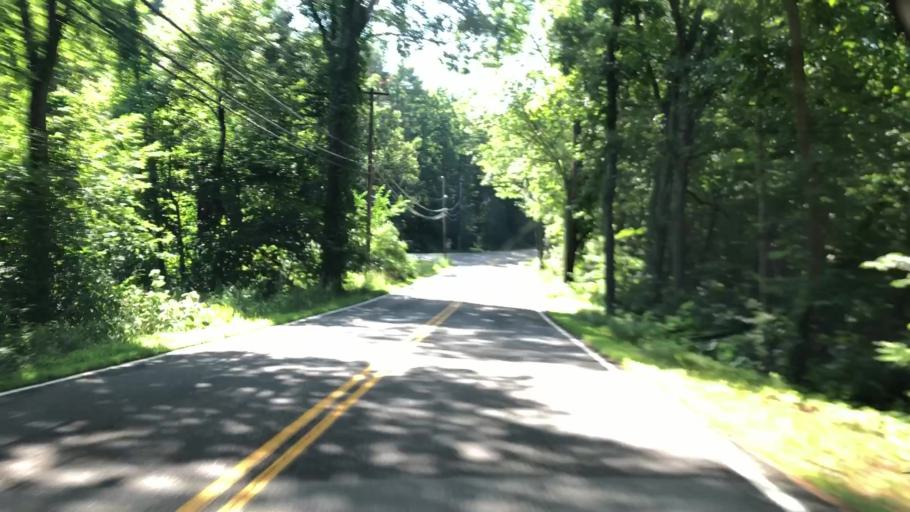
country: US
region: New Hampshire
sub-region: Hillsborough County
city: Milford
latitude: 42.8350
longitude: -71.5940
